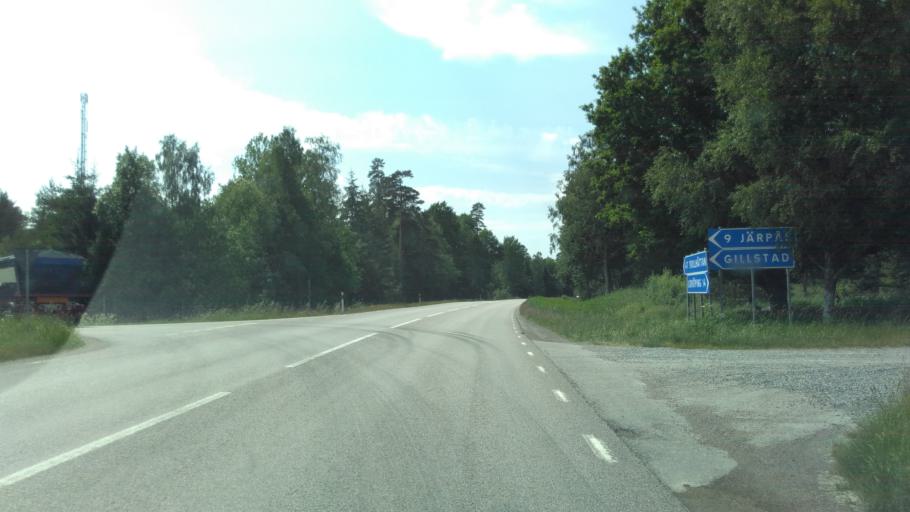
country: SE
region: Vaestra Goetaland
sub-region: Vara Kommun
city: Vara
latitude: 58.4438
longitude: 12.9647
